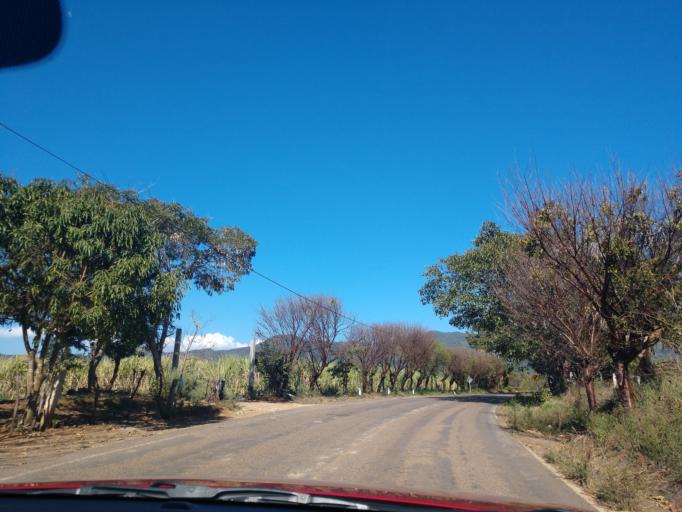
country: MX
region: Nayarit
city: Compostela
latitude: 21.2717
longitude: -104.8880
